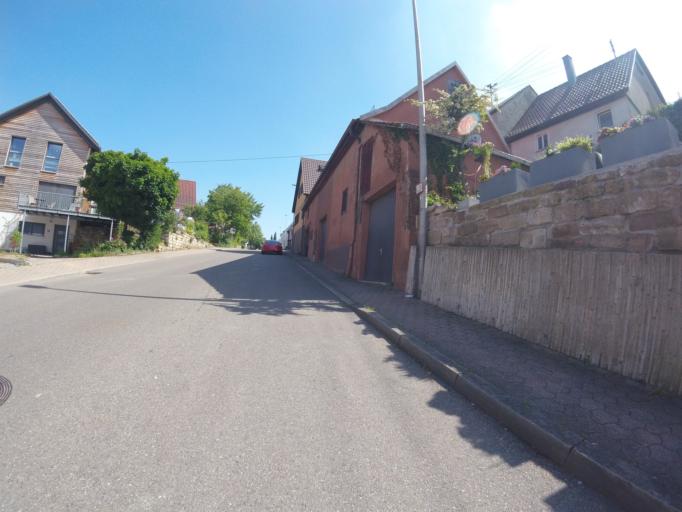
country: DE
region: Baden-Wuerttemberg
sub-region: Regierungsbezirk Stuttgart
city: Steinheim am der Murr
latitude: 48.9785
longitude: 9.2892
